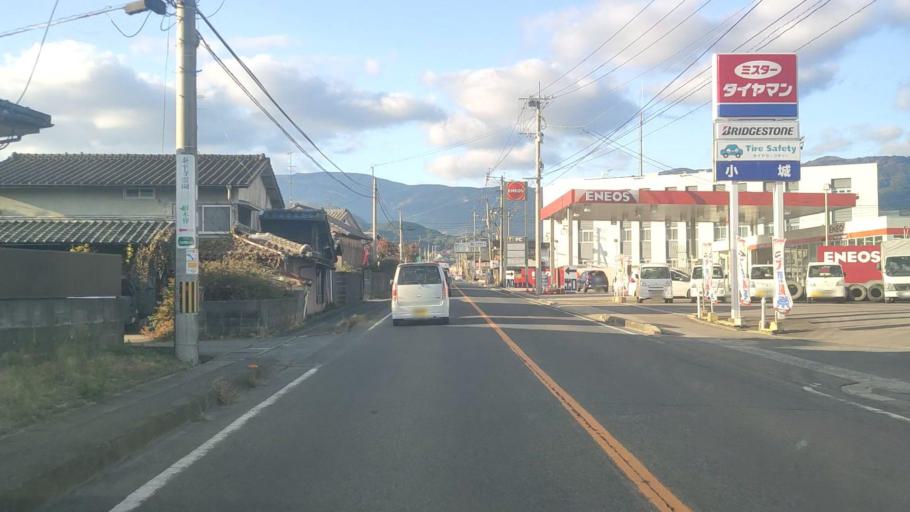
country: JP
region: Saga Prefecture
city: Saga-shi
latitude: 33.2885
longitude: 130.2060
